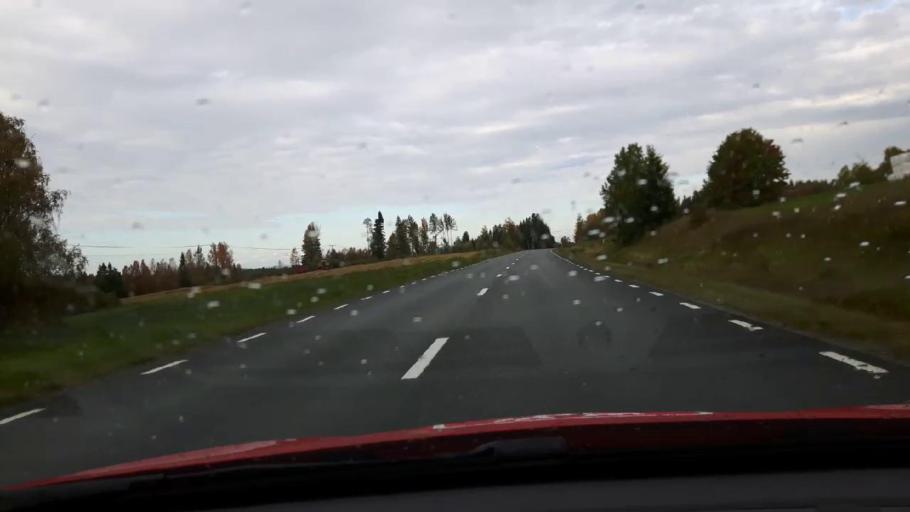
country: SE
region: Jaemtland
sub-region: Krokoms Kommun
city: Krokom
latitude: 63.1118
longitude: 14.2934
